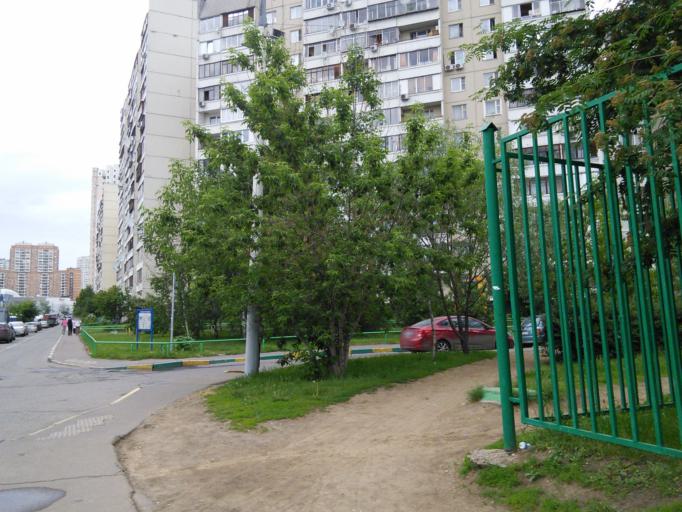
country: RU
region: Moscow
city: Brateyevo
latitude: 55.6567
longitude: 37.7541
